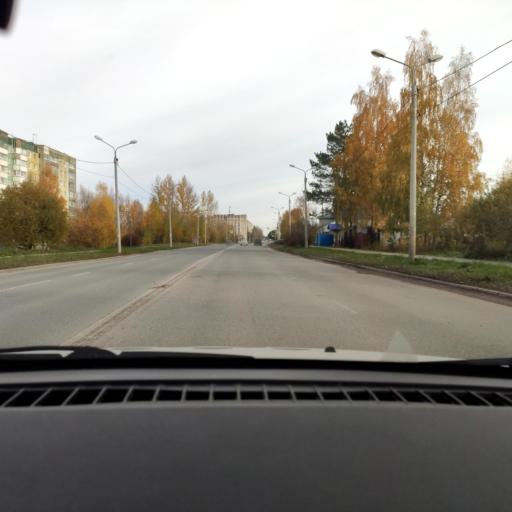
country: RU
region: Perm
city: Perm
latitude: 58.0546
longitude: 56.3553
